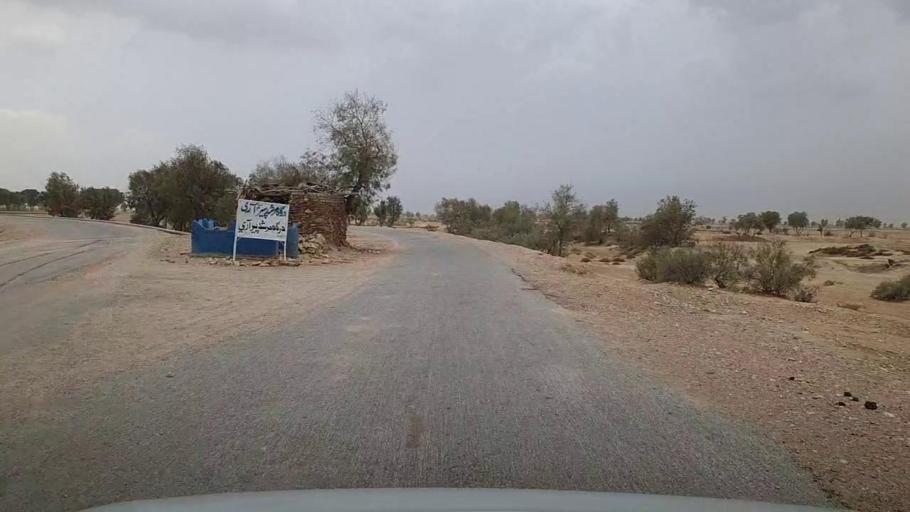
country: PK
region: Sindh
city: Sehwan
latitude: 26.3233
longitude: 67.7265
